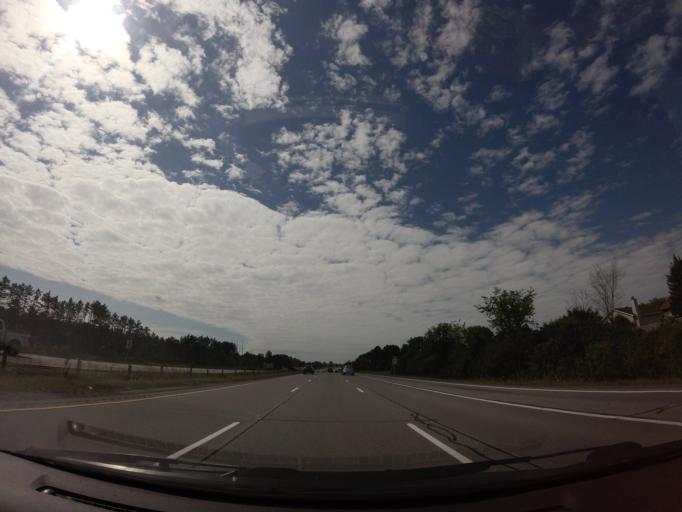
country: CA
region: Ontario
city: Ottawa
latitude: 45.4464
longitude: -75.5871
